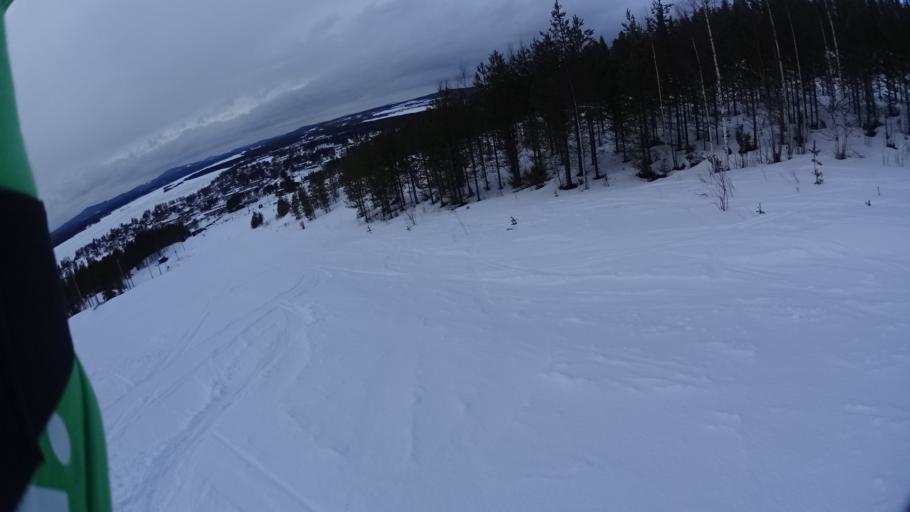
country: SE
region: Vaesterbotten
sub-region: Mala Kommun
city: Mala
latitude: 65.1785
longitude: 18.7592
